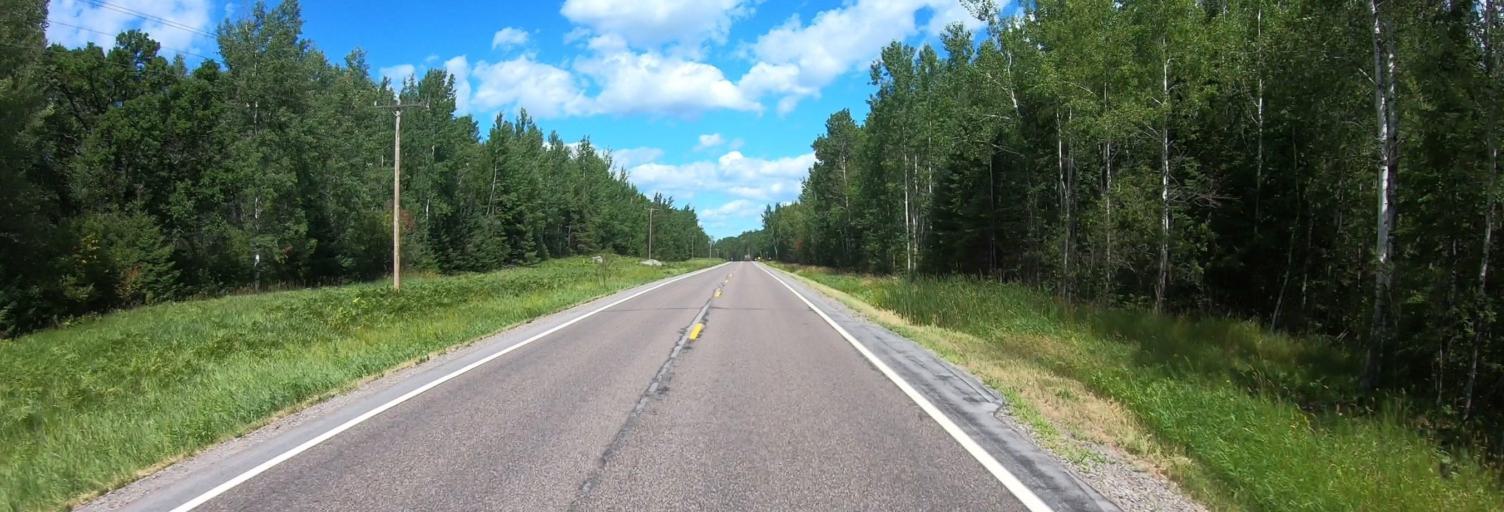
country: US
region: Minnesota
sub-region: Saint Louis County
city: Mountain Iron
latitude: 47.9151
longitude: -92.6567
